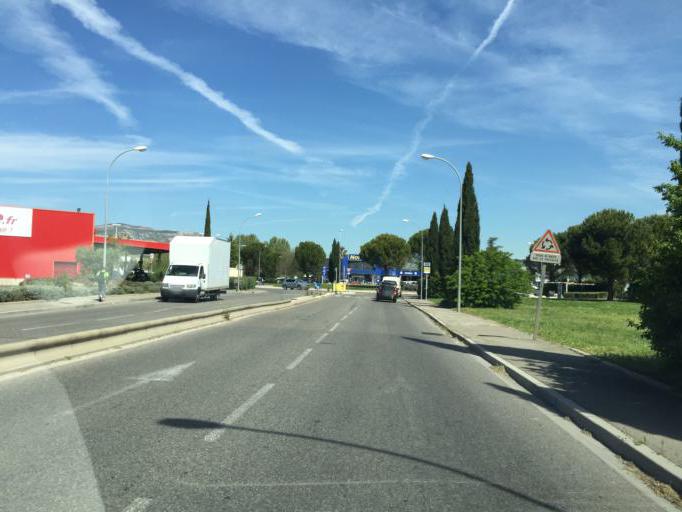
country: FR
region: Provence-Alpes-Cote d'Azur
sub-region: Departement des Bouches-du-Rhone
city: Aubagne
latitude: 43.2952
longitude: 5.5951
